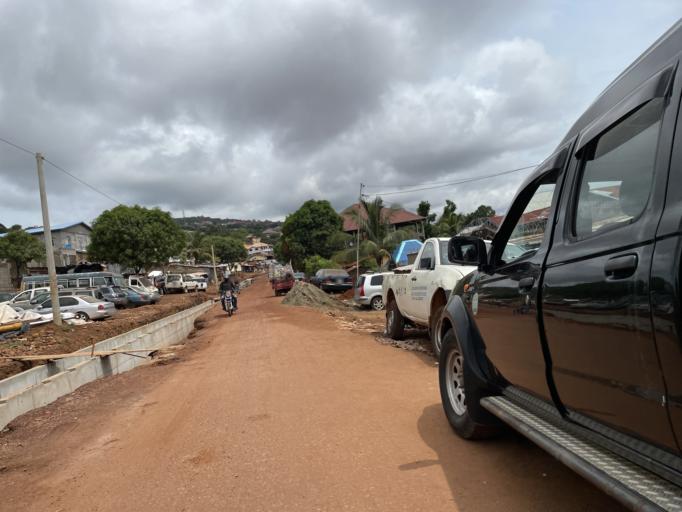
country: SL
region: Western Area
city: Hastings
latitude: 8.4132
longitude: -13.1516
